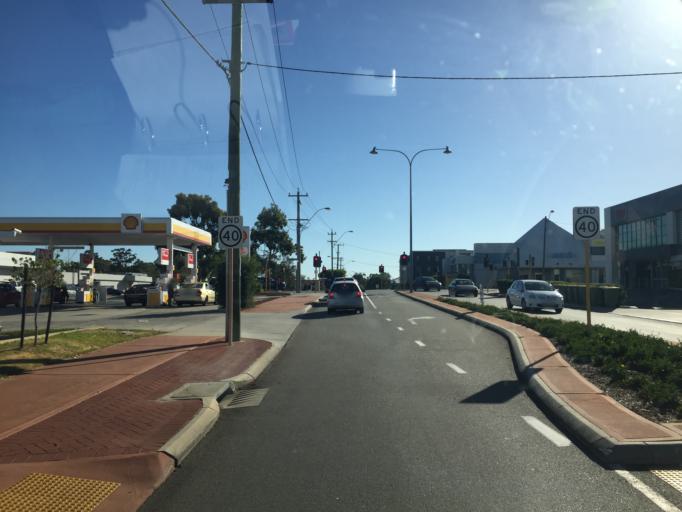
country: AU
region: Western Australia
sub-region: Belmont
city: Rivervale
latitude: -31.9646
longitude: 115.9333
